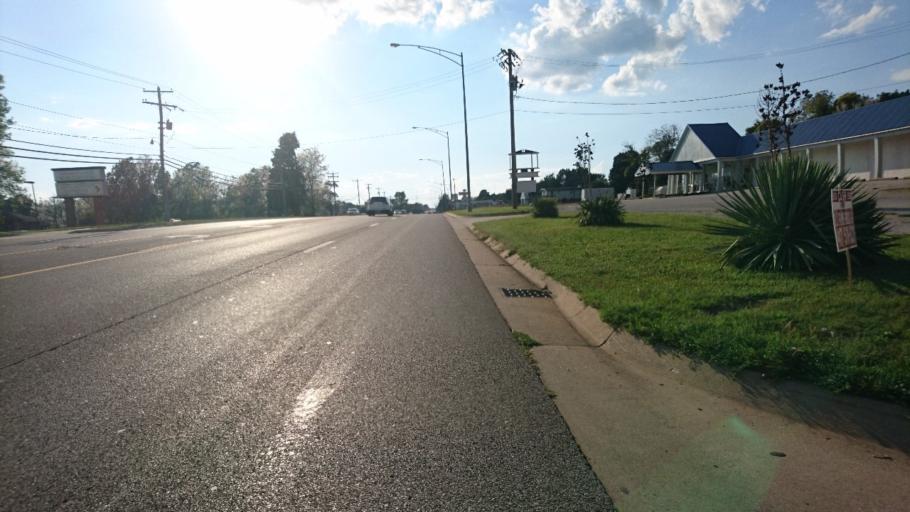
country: US
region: Missouri
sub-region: Greene County
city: Springfield
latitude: 37.2124
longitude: -93.3539
